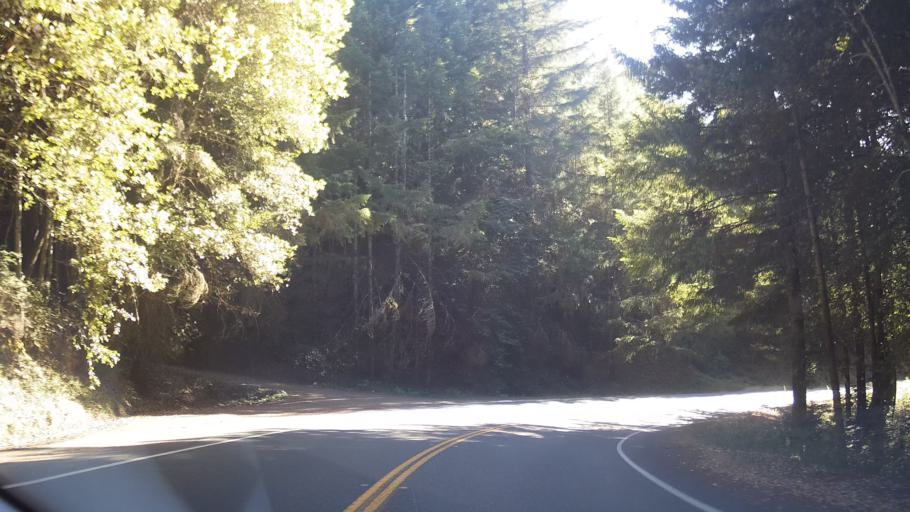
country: US
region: California
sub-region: Mendocino County
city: Brooktrails
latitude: 39.3856
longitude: -123.4713
